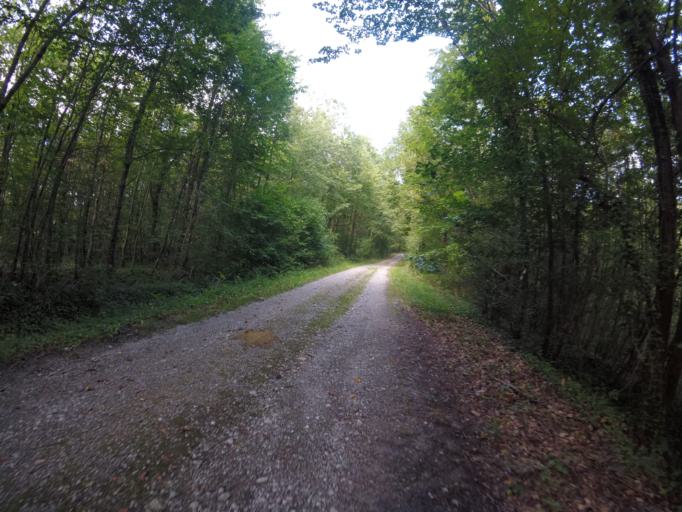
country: DE
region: Baden-Wuerttemberg
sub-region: Regierungsbezirk Stuttgart
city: Oppenweiler
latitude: 48.9683
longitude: 9.4857
